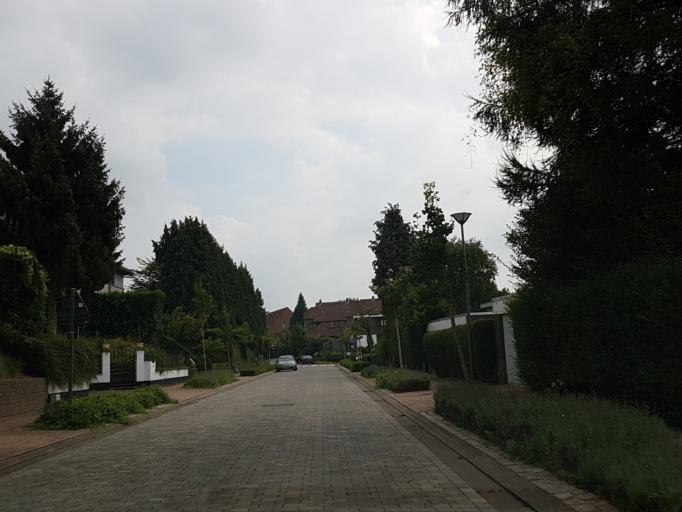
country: BE
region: Flanders
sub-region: Provincie Vlaams-Brabant
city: Zaventem
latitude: 50.8778
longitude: 4.4762
